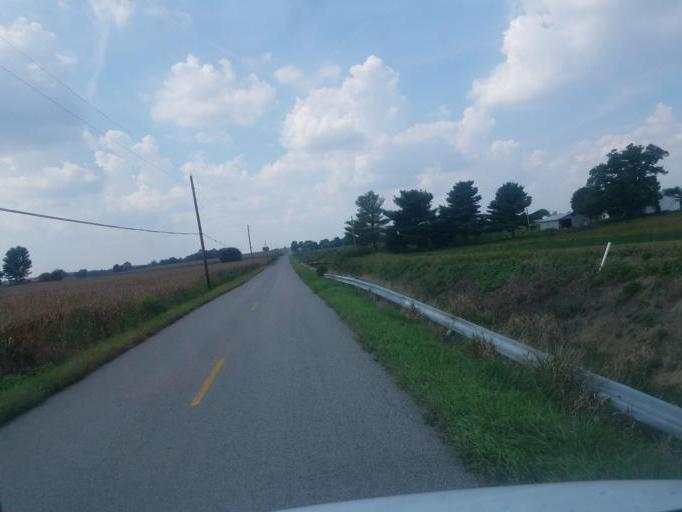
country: US
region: Ohio
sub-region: Logan County
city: Northwood
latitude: 40.6159
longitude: -83.7815
